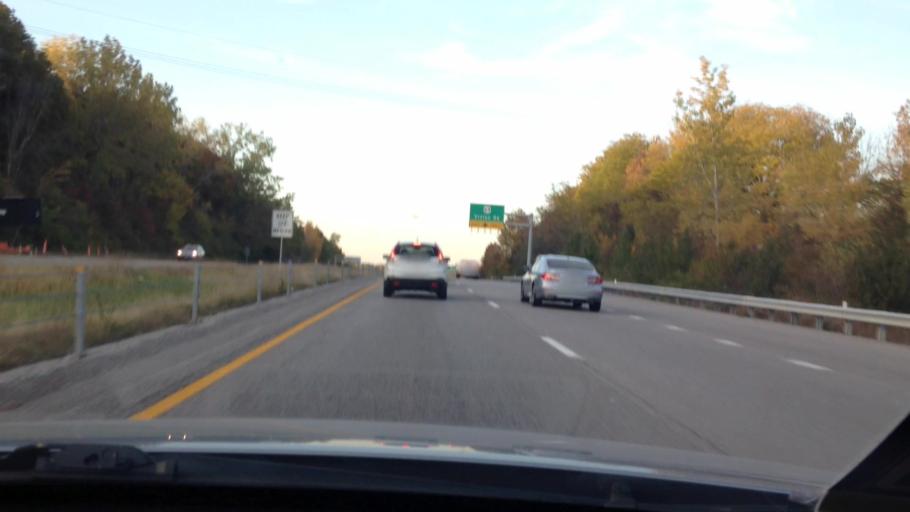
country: US
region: Missouri
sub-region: Platte County
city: Riverside
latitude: 39.1734
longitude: -94.5947
